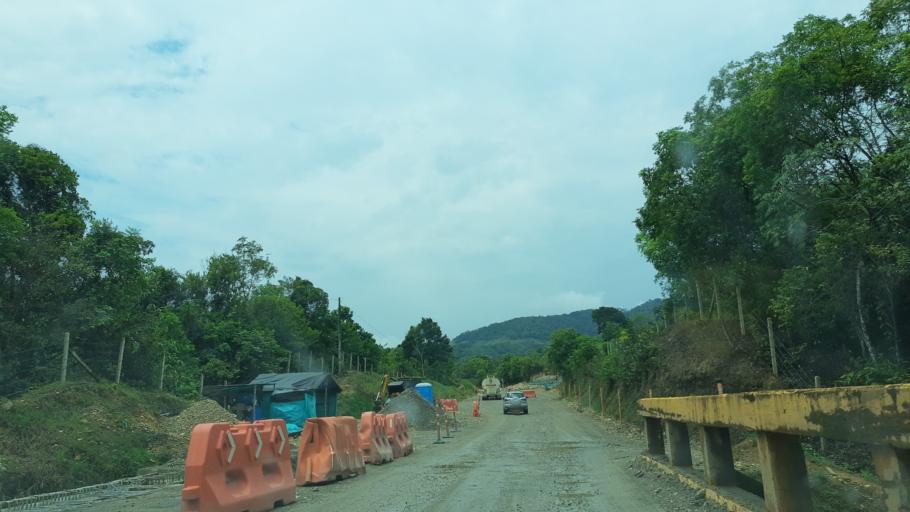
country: CO
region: Casanare
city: Sabanalarga
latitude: 4.7755
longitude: -73.0023
